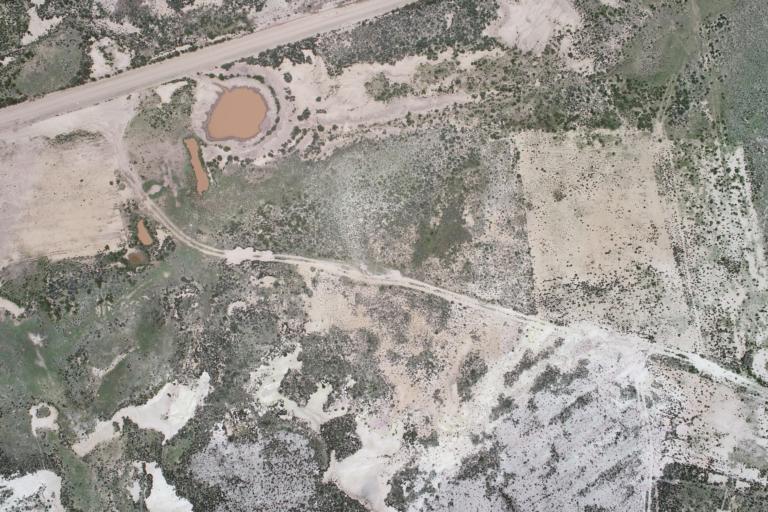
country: BO
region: La Paz
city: Patacamaya
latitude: -17.2822
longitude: -68.4949
